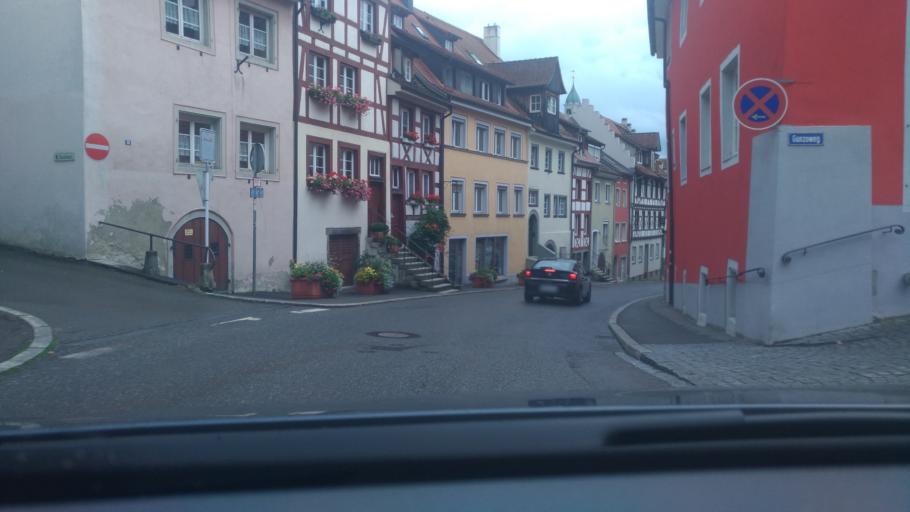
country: DE
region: Baden-Wuerttemberg
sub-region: Tuebingen Region
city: Uberlingen
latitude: 47.7694
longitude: 9.1591
